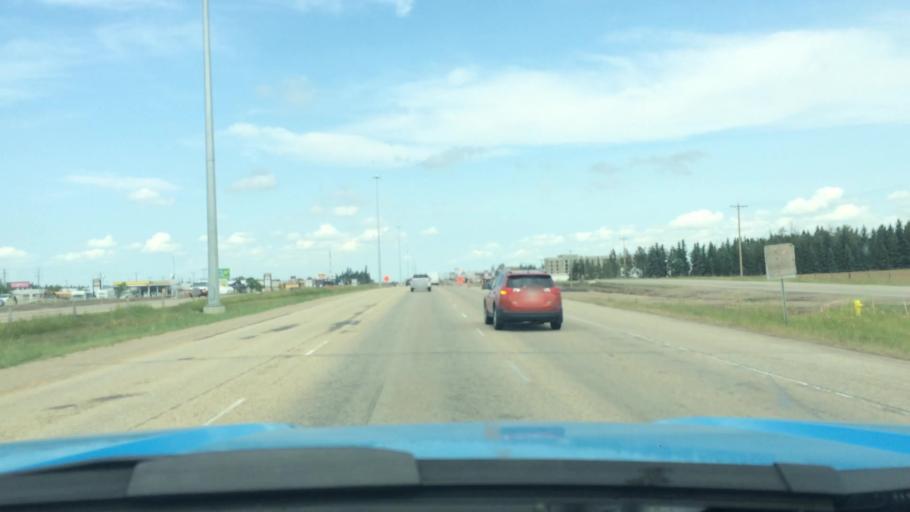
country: CA
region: Alberta
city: Red Deer
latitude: 52.2082
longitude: -113.8138
